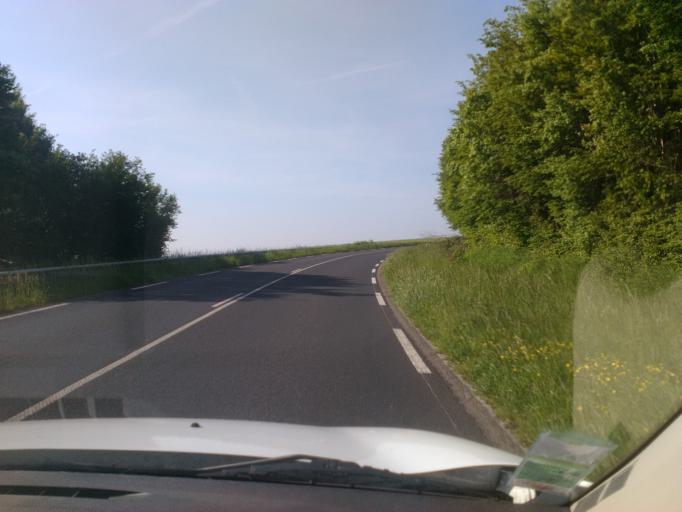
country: FR
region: Lorraine
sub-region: Departement des Vosges
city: Mirecourt
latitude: 48.3363
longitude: 6.1403
